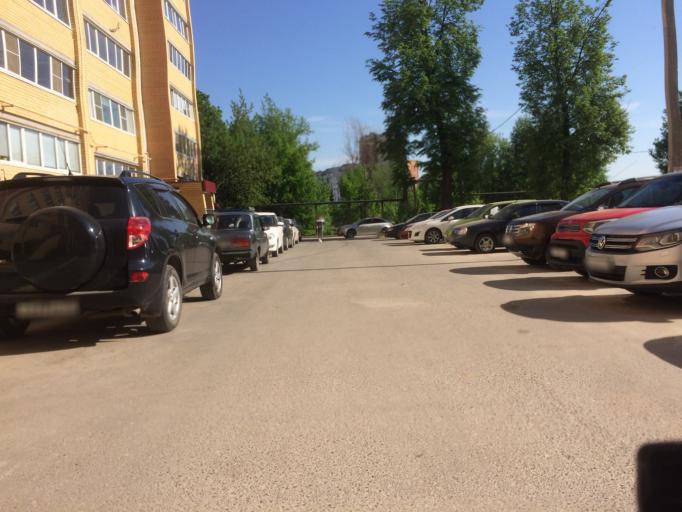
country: RU
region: Mariy-El
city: Yoshkar-Ola
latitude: 56.6465
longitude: 47.8525
